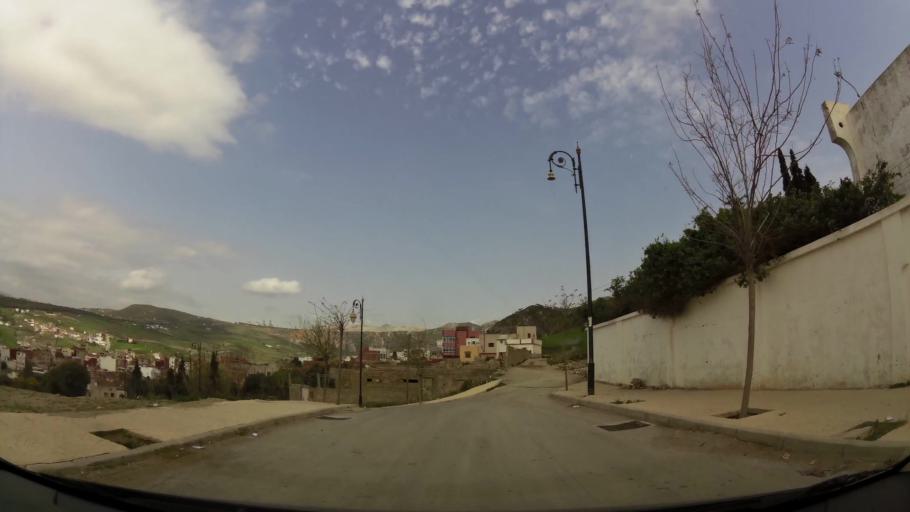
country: MA
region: Tanger-Tetouan
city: Tetouan
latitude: 35.5794
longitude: -5.3946
